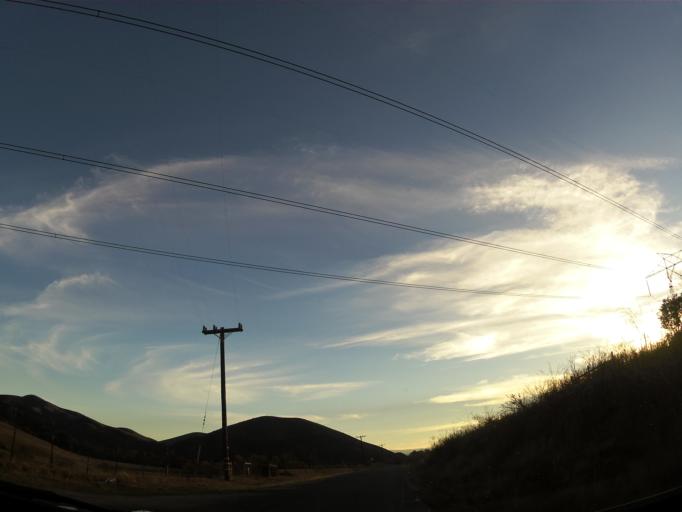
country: US
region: California
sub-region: San Benito County
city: San Juan Bautista
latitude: 36.7863
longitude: -121.5897
